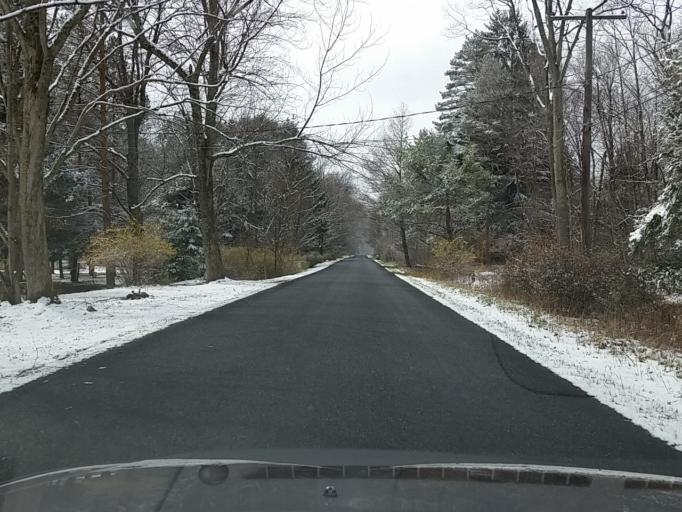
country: US
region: Pennsylvania
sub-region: Sullivan County
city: Laporte
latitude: 41.3056
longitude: -76.4177
